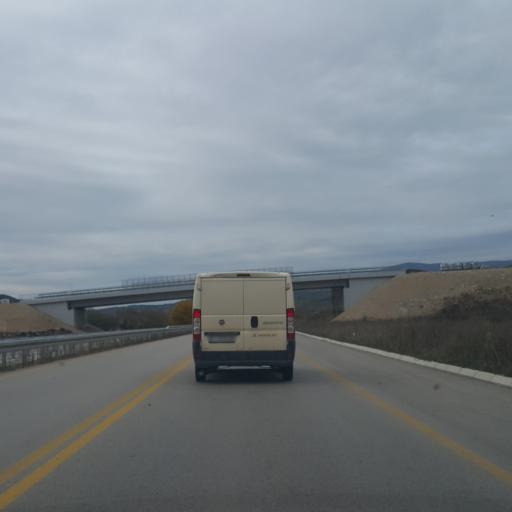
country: RS
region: Central Serbia
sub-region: Pirotski Okrug
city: Pirot
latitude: 43.2244
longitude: 22.4753
